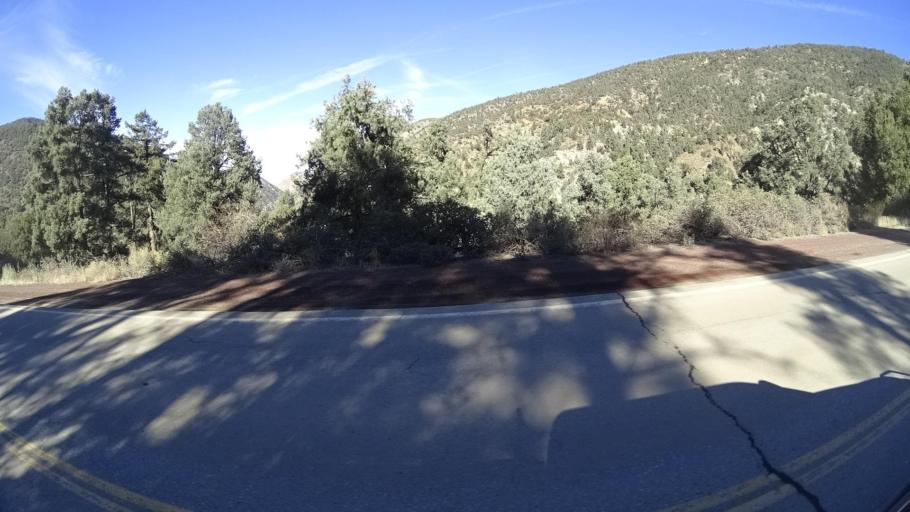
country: US
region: California
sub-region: Kern County
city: Pine Mountain Club
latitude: 34.8522
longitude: -119.1210
